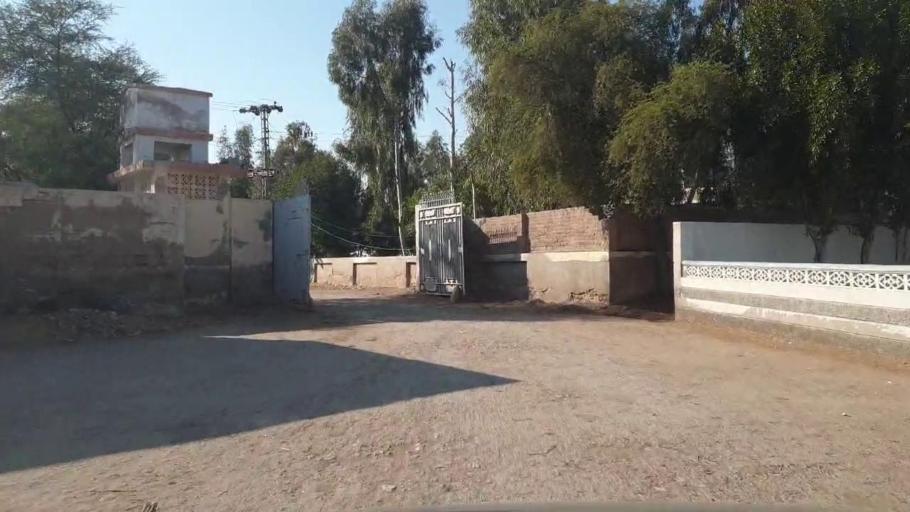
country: PK
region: Sindh
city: Shahpur Chakar
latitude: 26.1768
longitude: 68.6772
